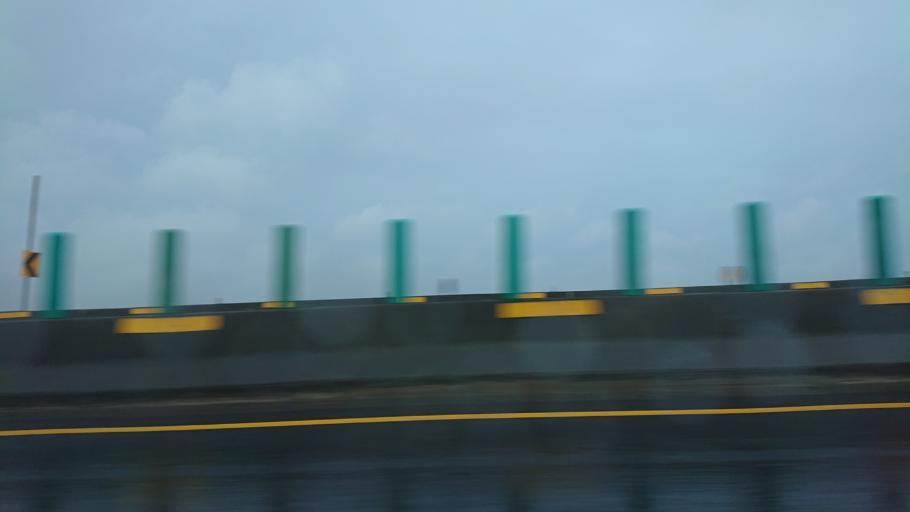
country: TW
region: Taiwan
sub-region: Changhua
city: Chang-hua
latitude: 24.1604
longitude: 120.4633
